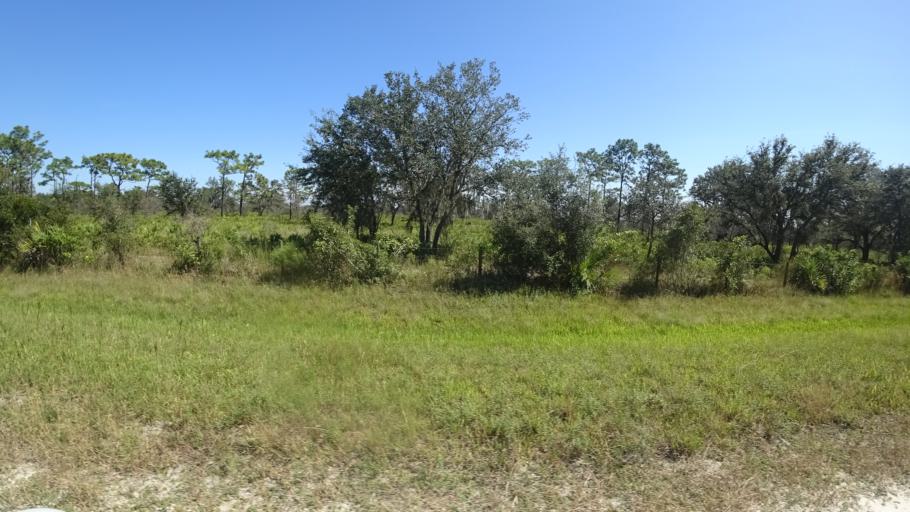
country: US
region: Florida
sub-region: DeSoto County
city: Arcadia
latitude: 27.3221
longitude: -82.0804
